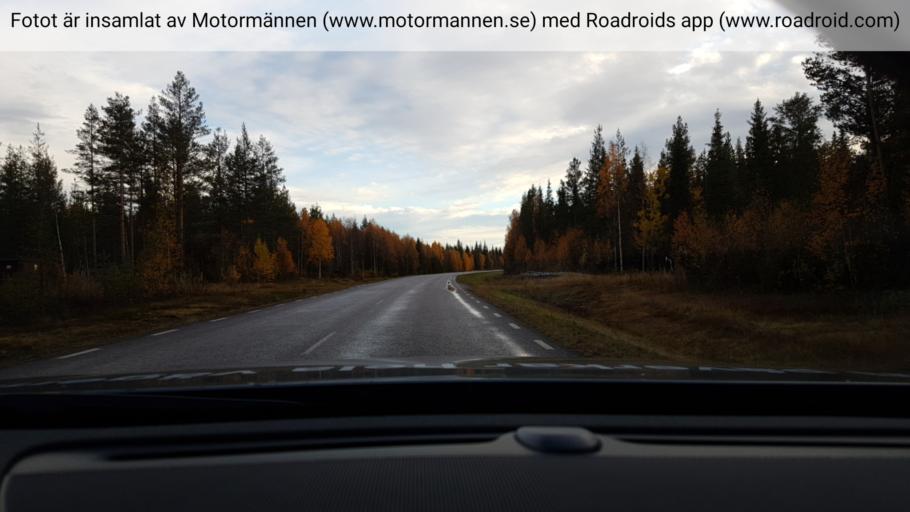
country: SE
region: Norrbotten
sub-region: Overkalix Kommun
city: OEverkalix
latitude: 66.9063
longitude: 22.7759
